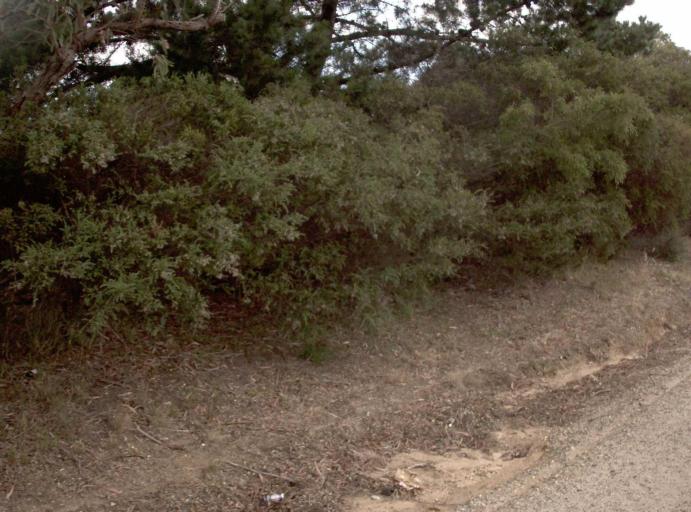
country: AU
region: Victoria
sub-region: Wellington
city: Sale
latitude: -38.1866
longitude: 147.0921
